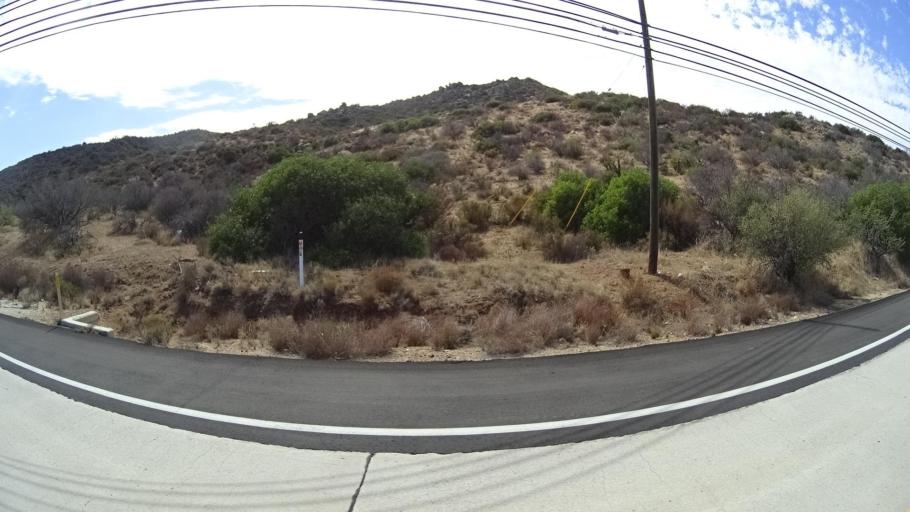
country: MX
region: Baja California
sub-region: Tecate
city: Cereso del Hongo
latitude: 32.6396
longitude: -116.2284
